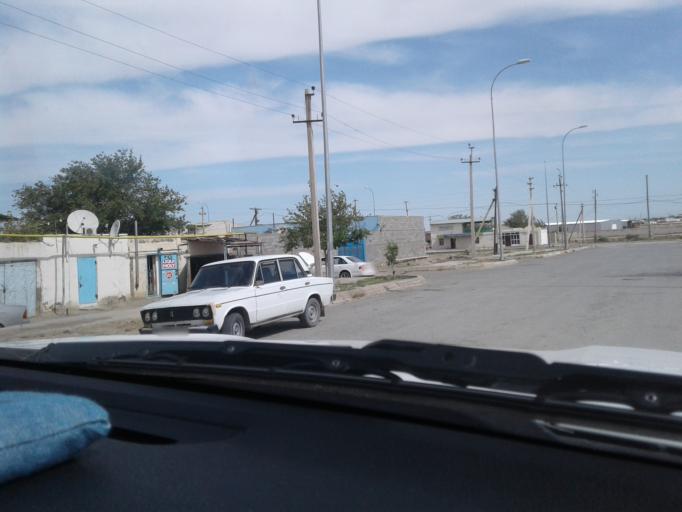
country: TM
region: Balkan
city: Gazanjyk
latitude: 39.2441
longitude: 55.5038
